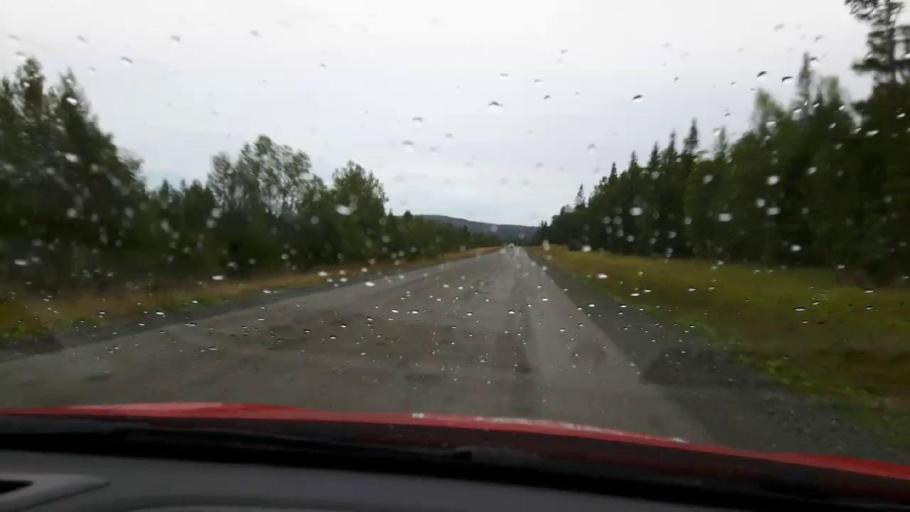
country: NO
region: Nord-Trondelag
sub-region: Meraker
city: Meraker
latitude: 63.5588
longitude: 12.3085
